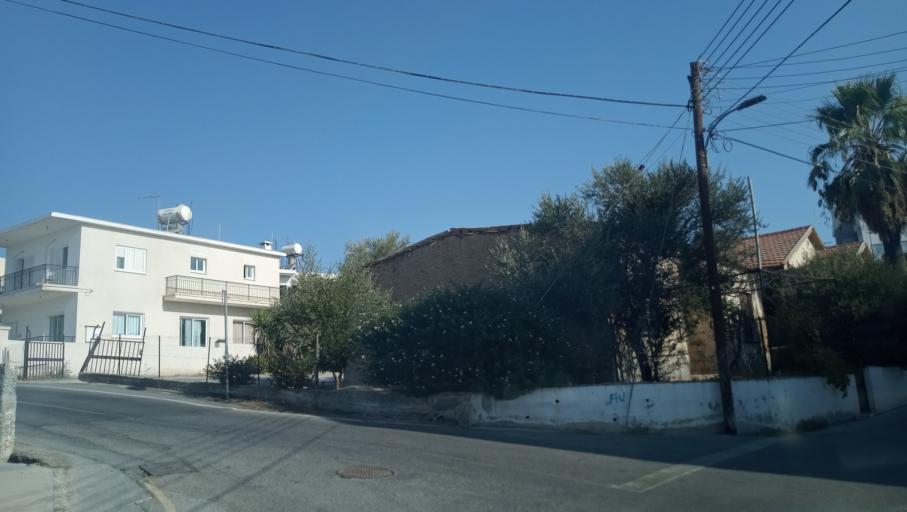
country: CY
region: Lefkosia
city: Geri
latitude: 35.1087
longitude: 33.4224
